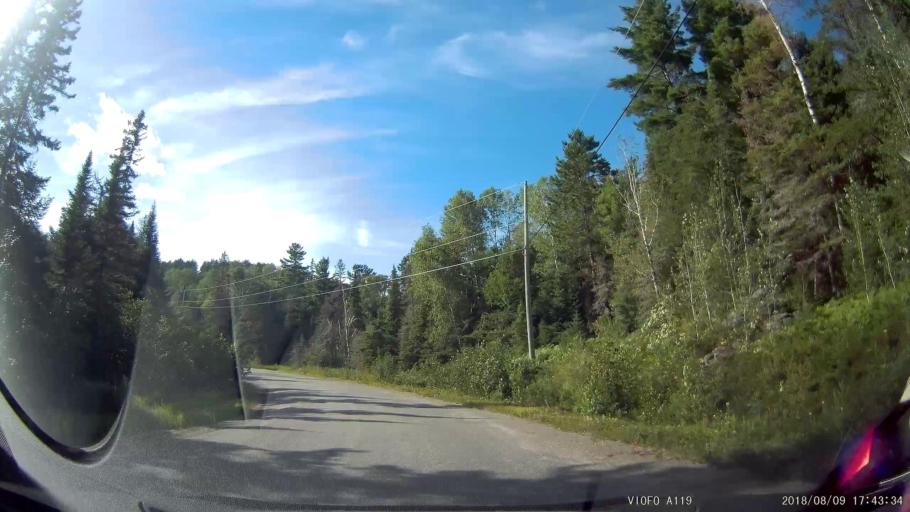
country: CA
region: Ontario
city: Rayside-Balfour
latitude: 46.6085
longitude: -81.5288
